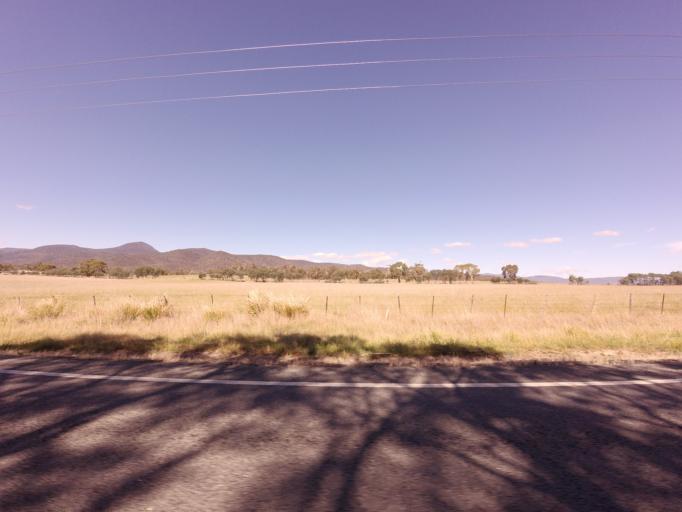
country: AU
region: Tasmania
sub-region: Northern Midlands
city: Evandale
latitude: -41.7632
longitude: 147.7482
